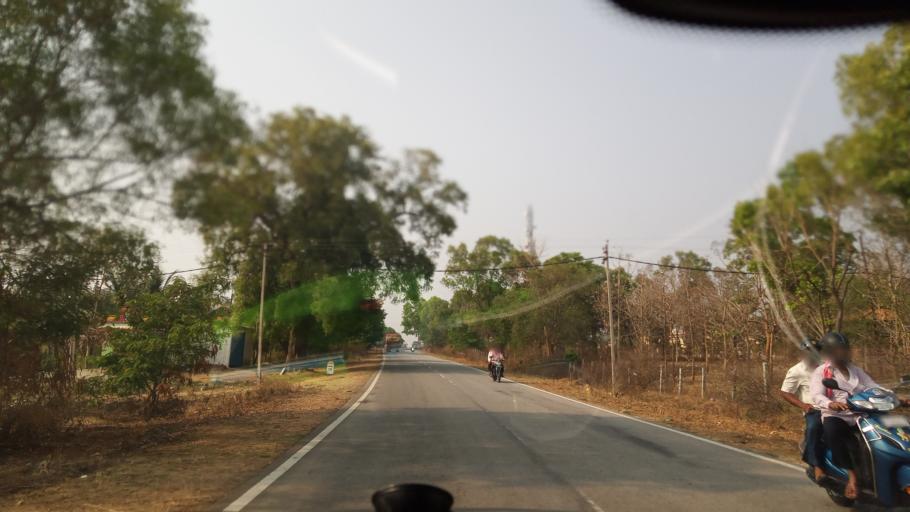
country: IN
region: Karnataka
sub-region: Mandya
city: Belluru
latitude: 12.9480
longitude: 76.7516
